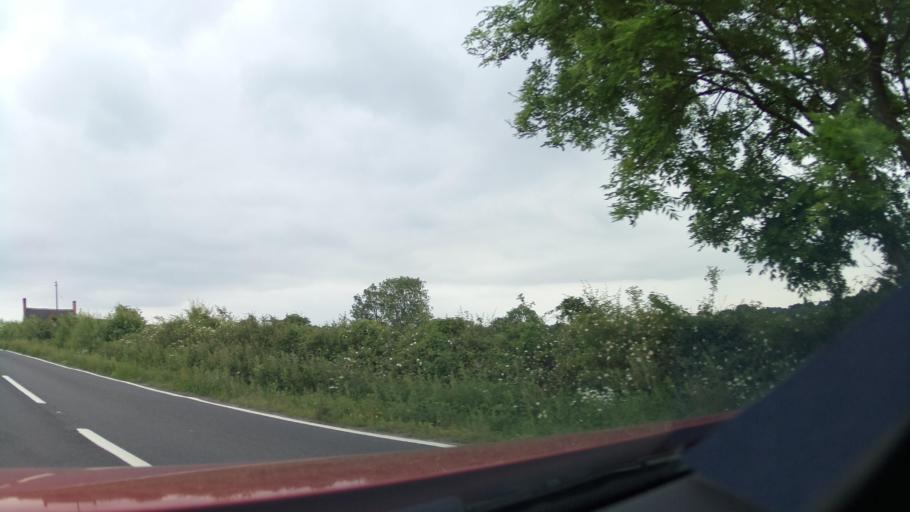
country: GB
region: England
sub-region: Staffordshire
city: Mayfield
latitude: 52.9557
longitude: -1.7583
